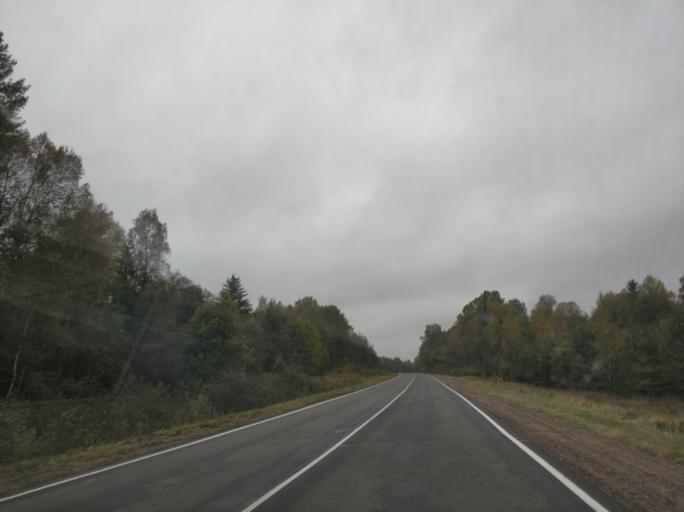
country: BY
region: Vitebsk
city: Rasony
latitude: 56.1039
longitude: 28.7233
